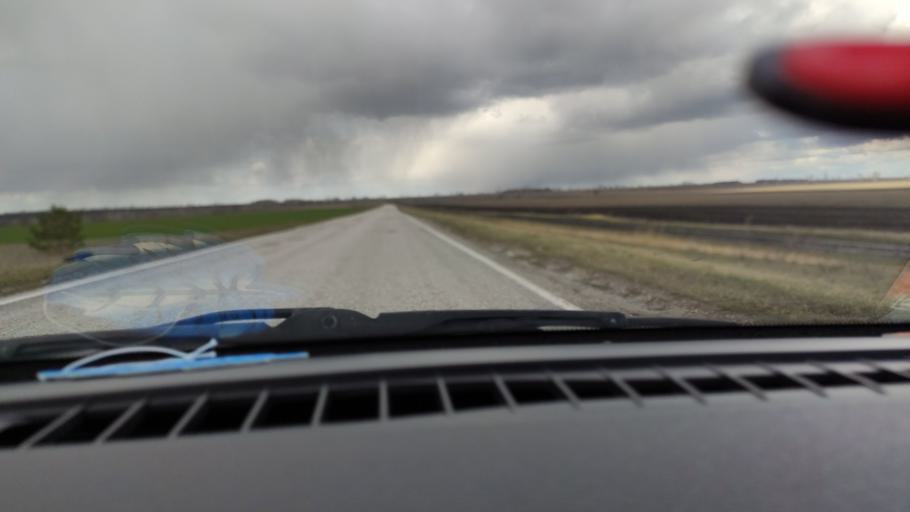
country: RU
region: Samara
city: Povolzhskiy
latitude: 53.7938
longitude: 49.7317
